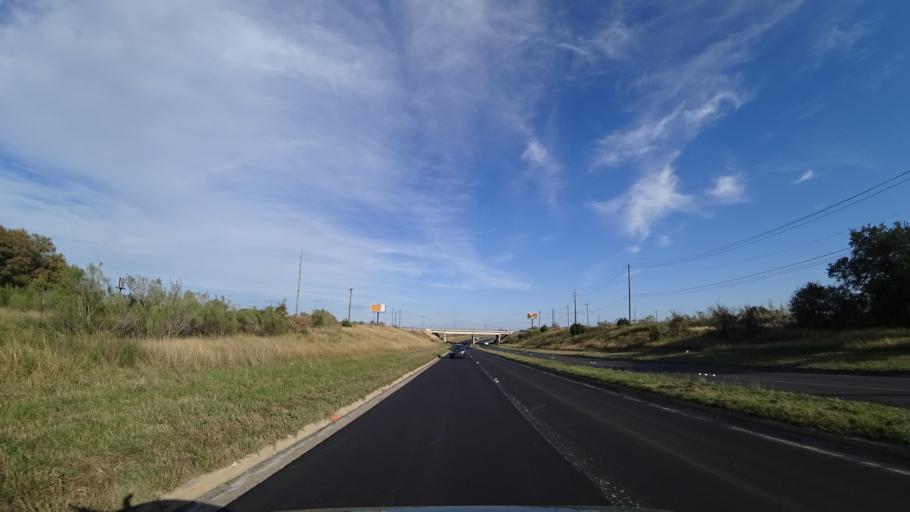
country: US
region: Texas
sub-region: Travis County
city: Wells Branch
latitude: 30.4493
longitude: -97.7201
